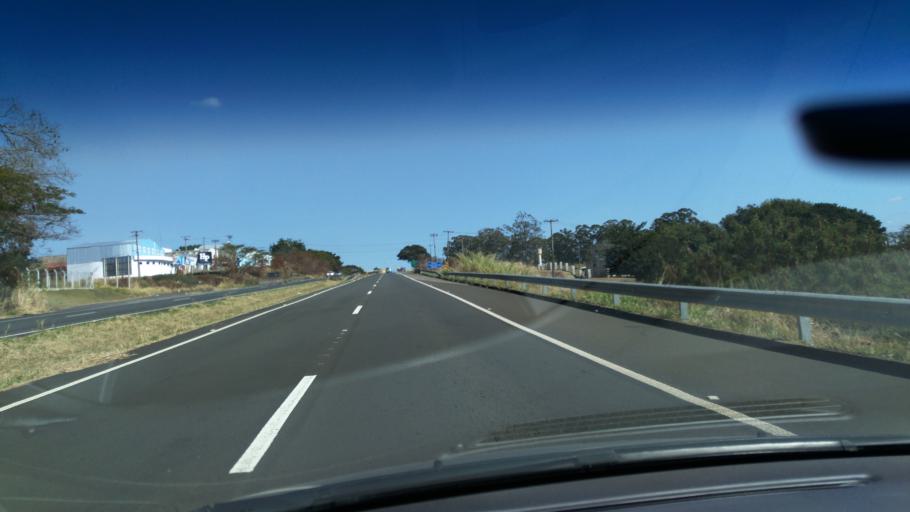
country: BR
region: Sao Paulo
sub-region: Santo Antonio Do Jardim
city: Espirito Santo do Pinhal
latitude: -22.1733
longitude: -46.7463
